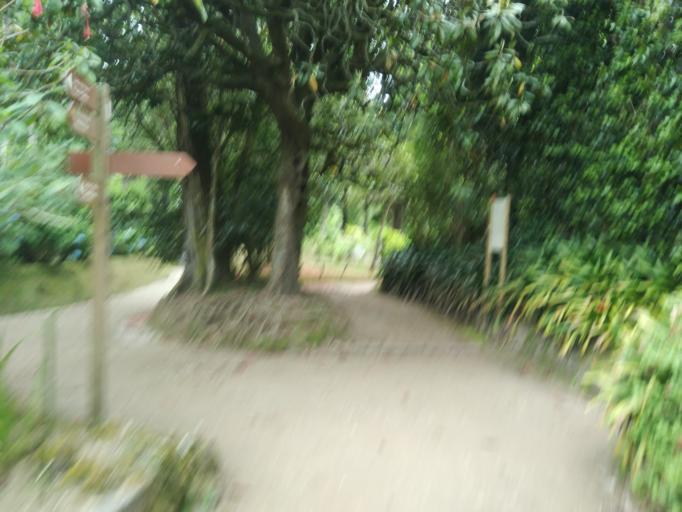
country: PT
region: Azores
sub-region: Povoacao
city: Furnas
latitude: 37.7702
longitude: -25.3136
